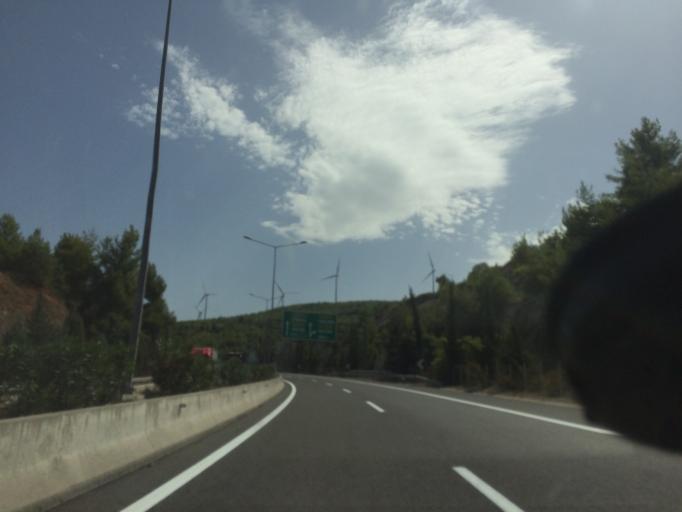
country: GR
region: Central Greece
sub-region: Nomos Fthiotidos
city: Martinon
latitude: 38.6022
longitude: 23.1790
